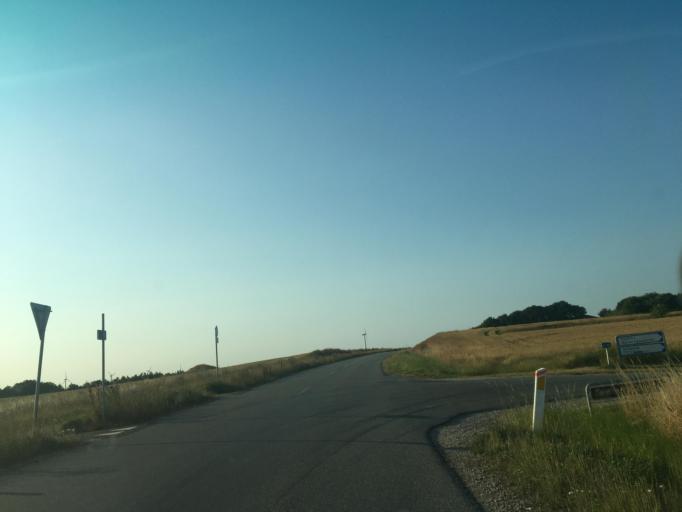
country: DK
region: North Denmark
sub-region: Thisted Kommune
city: Hurup
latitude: 56.7651
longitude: 8.4214
